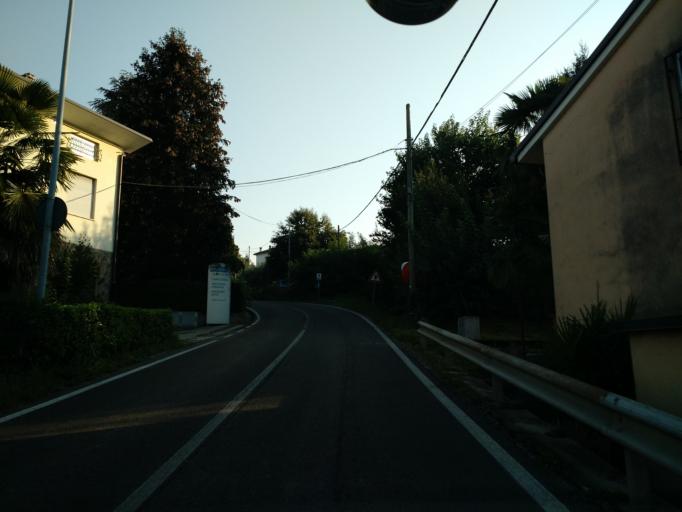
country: IT
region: Veneto
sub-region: Provincia di Vicenza
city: Fara Vicentino
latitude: 45.7382
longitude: 11.5605
